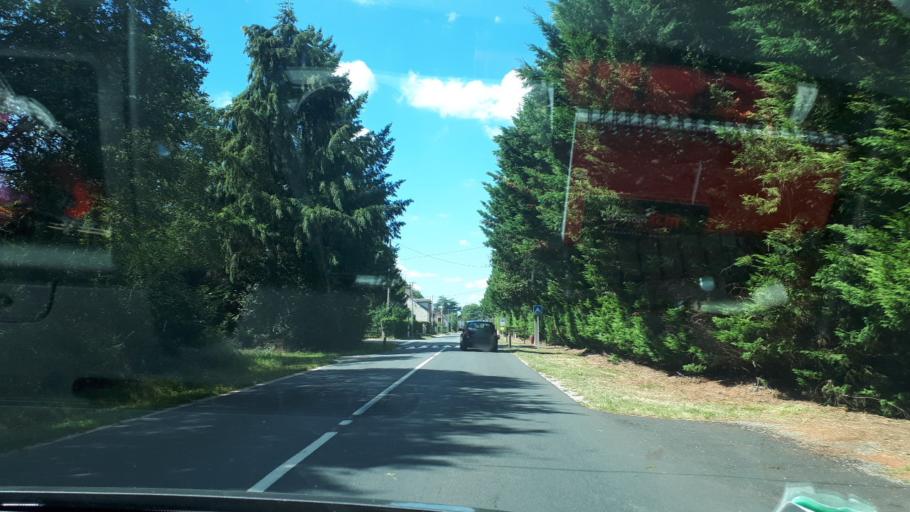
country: FR
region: Centre
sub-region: Departement du Loir-et-Cher
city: Neung-sur-Beuvron
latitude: 47.5453
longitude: 1.8588
